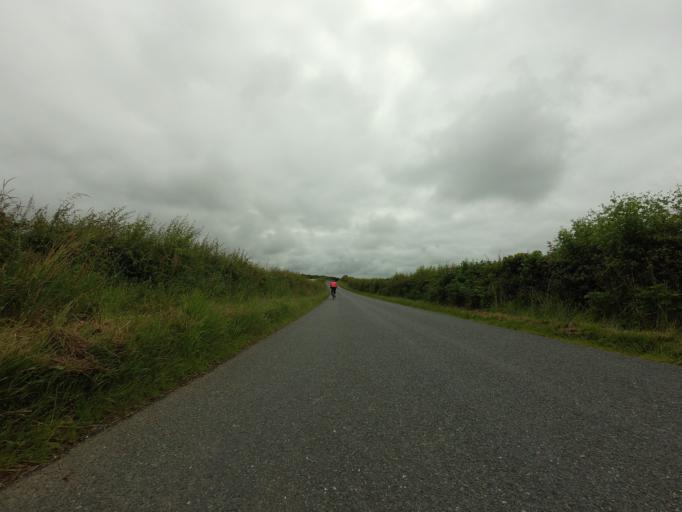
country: GB
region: Scotland
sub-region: Aberdeenshire
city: Rosehearty
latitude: 57.5356
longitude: -2.1796
